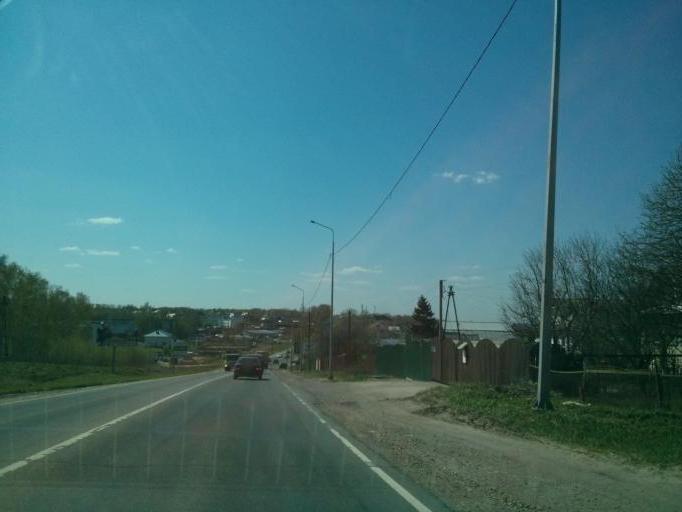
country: RU
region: Nizjnij Novgorod
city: Burevestnik
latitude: 56.2086
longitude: 43.8845
